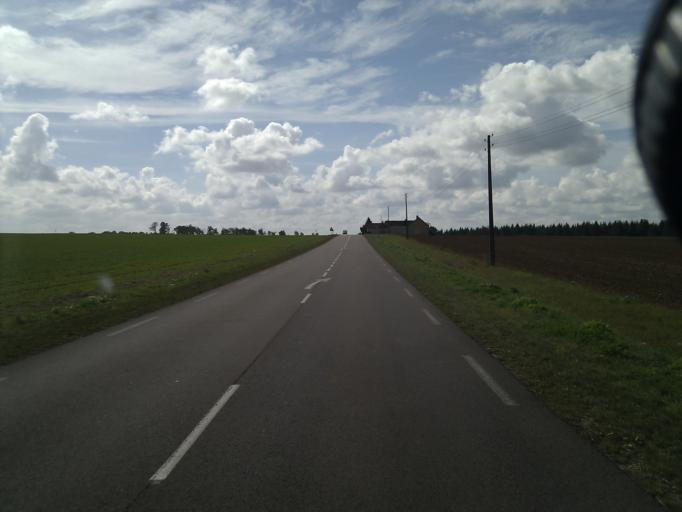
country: FR
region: Bourgogne
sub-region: Departement de la Cote-d'Or
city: Chatillon-sur-Seine
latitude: 47.8347
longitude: 4.5465
